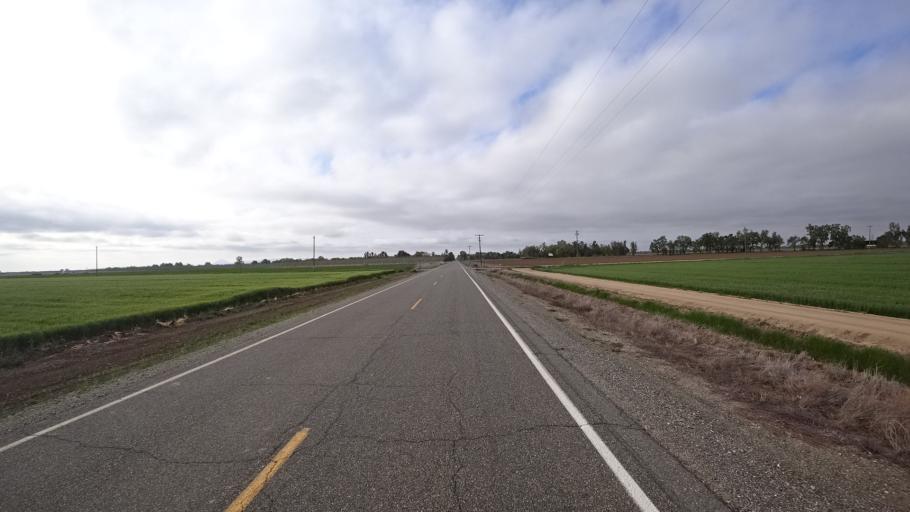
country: US
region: California
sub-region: Colusa County
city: Colusa
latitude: 39.4282
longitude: -121.9669
